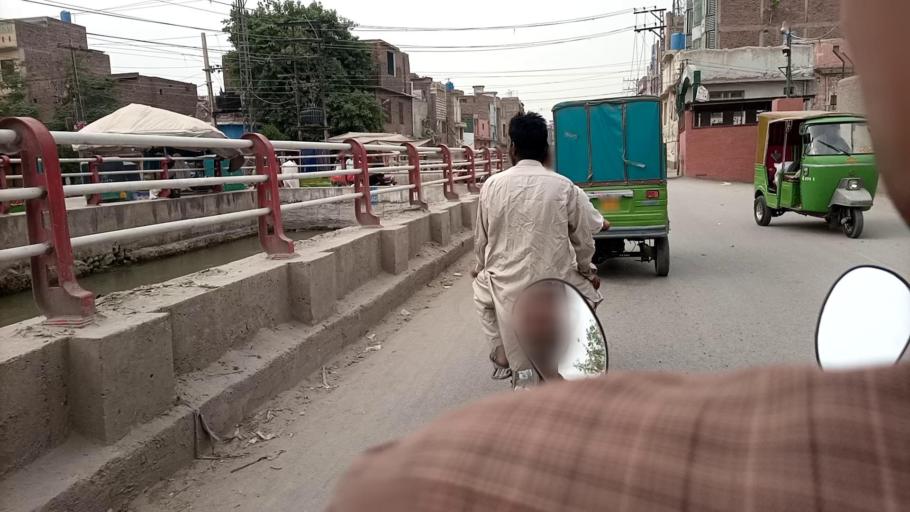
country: PK
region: Khyber Pakhtunkhwa
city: Peshawar
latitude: 34.0191
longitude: 71.5927
